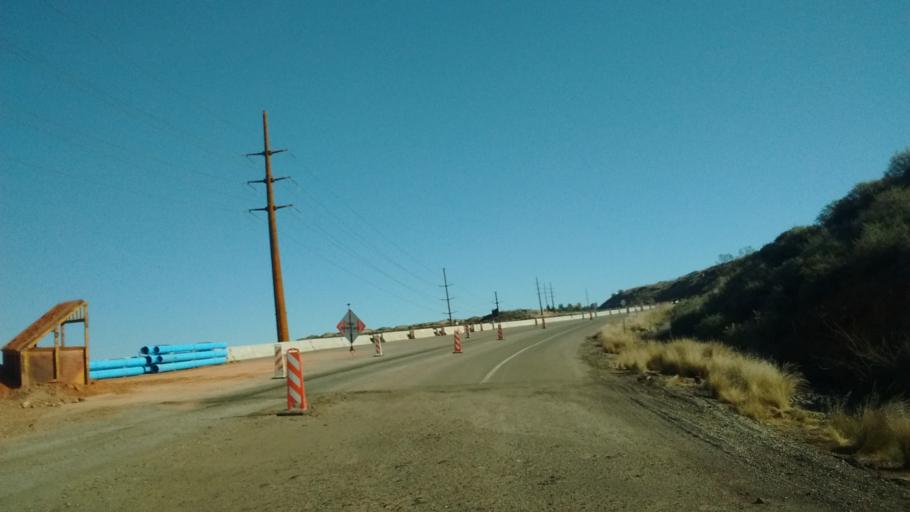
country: US
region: Utah
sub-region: Washington County
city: Washington
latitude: 37.1355
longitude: -113.4772
